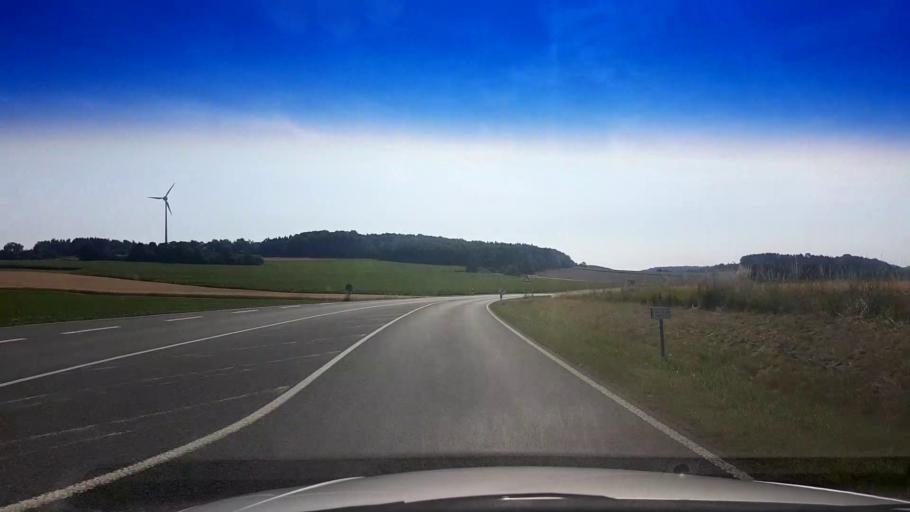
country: DE
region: Bavaria
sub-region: Upper Franconia
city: Hollfeld
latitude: 49.9478
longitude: 11.3267
